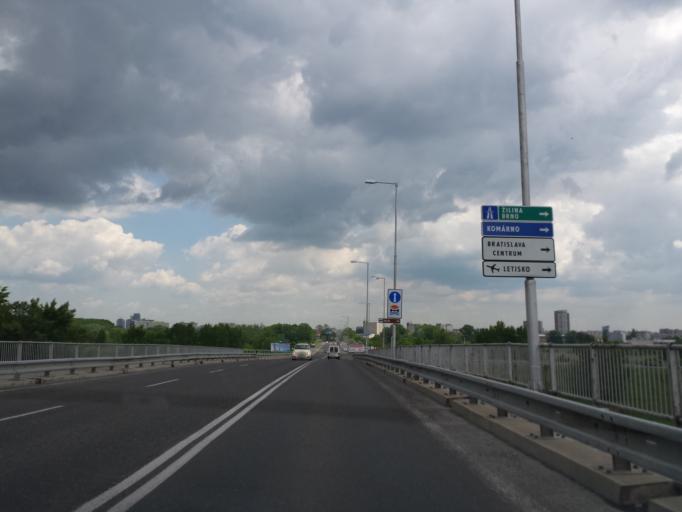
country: AT
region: Burgenland
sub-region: Politischer Bezirk Neusiedl am See
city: Kittsee
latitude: 48.1236
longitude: 17.0764
